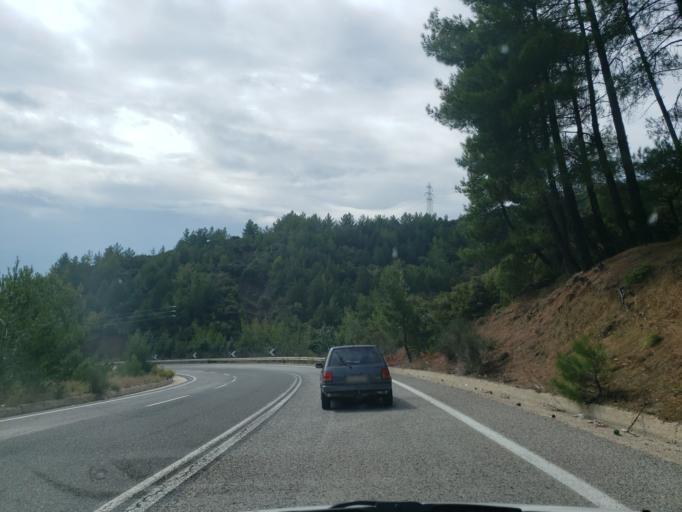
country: GR
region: Central Greece
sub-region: Nomos Fthiotidos
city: Stavros
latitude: 38.9840
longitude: 22.3793
